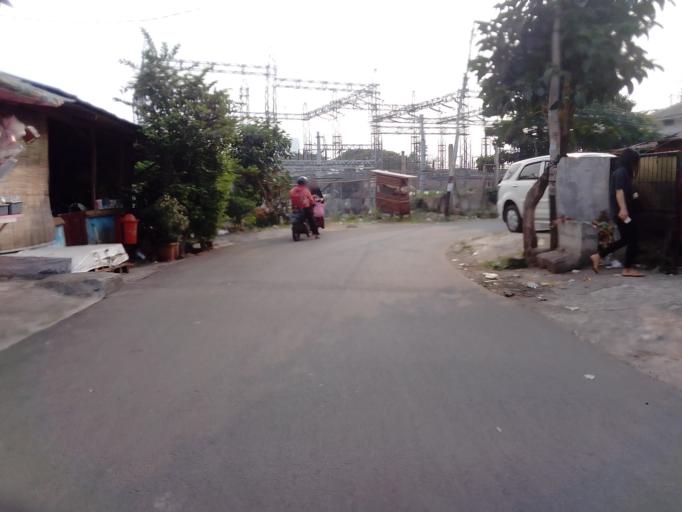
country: ID
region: Jakarta Raya
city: Jakarta
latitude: -6.1994
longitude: 106.8129
